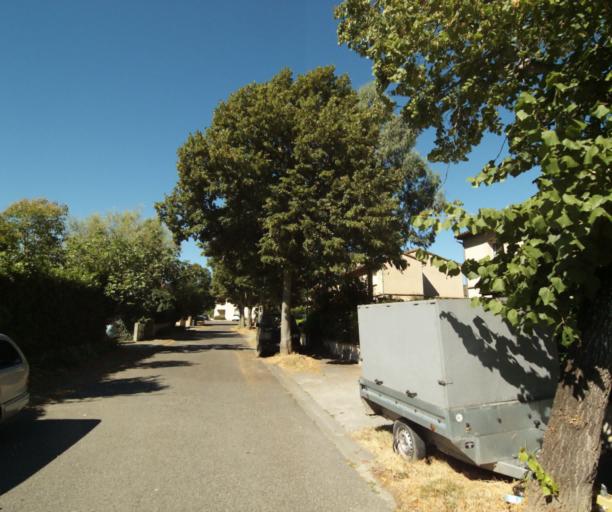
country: FR
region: Midi-Pyrenees
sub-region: Departement de la Haute-Garonne
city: Castanet-Tolosan
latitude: 43.5251
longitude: 1.4972
